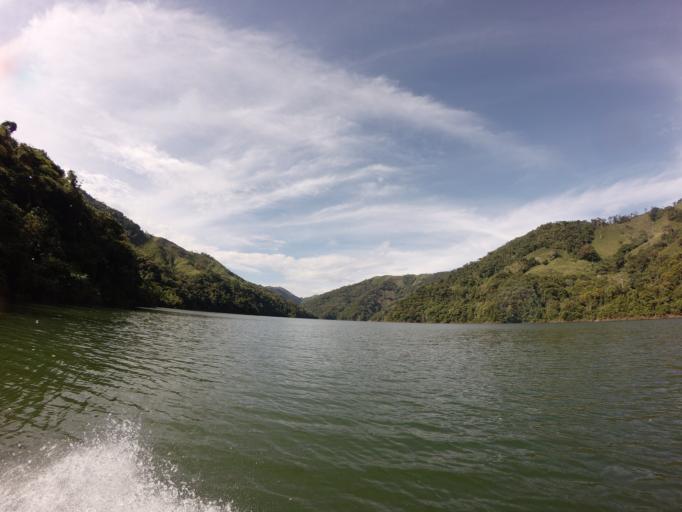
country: CO
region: Caldas
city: Norcasia
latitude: 5.5370
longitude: -74.9190
